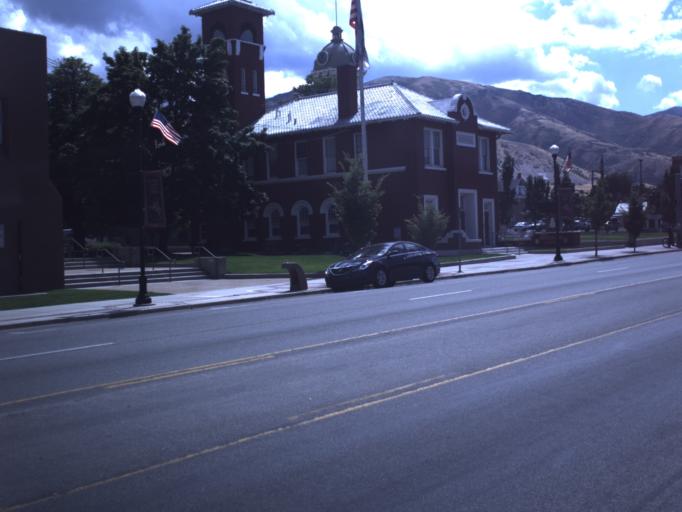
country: US
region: Utah
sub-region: Box Elder County
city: Brigham City
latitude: 41.5111
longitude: -112.0158
